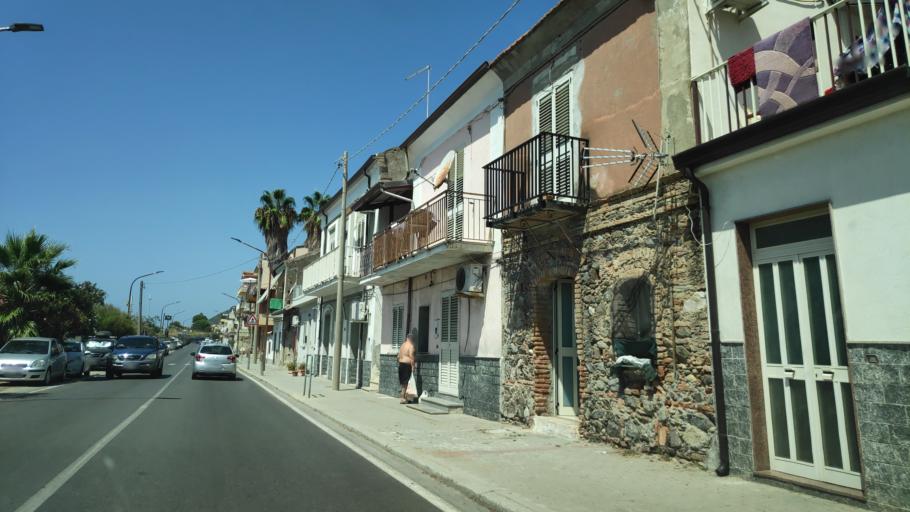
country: IT
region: Calabria
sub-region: Provincia di Reggio Calabria
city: Palizzi Marina
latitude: 37.9186
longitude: 15.9915
